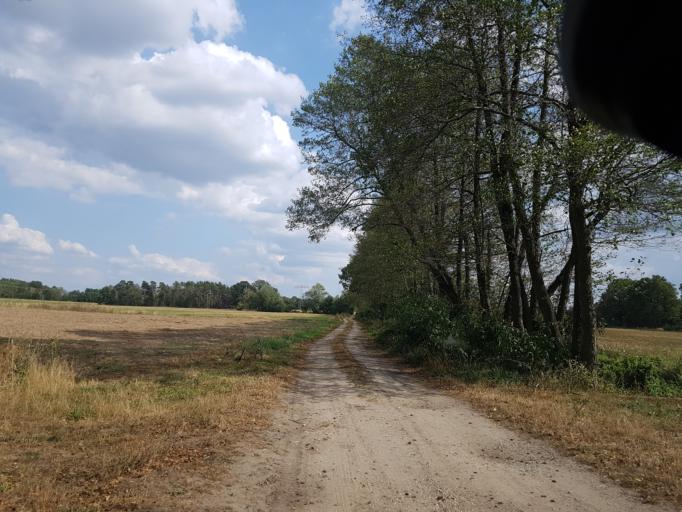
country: DE
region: Brandenburg
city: Calau
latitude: 51.7716
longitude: 13.9652
